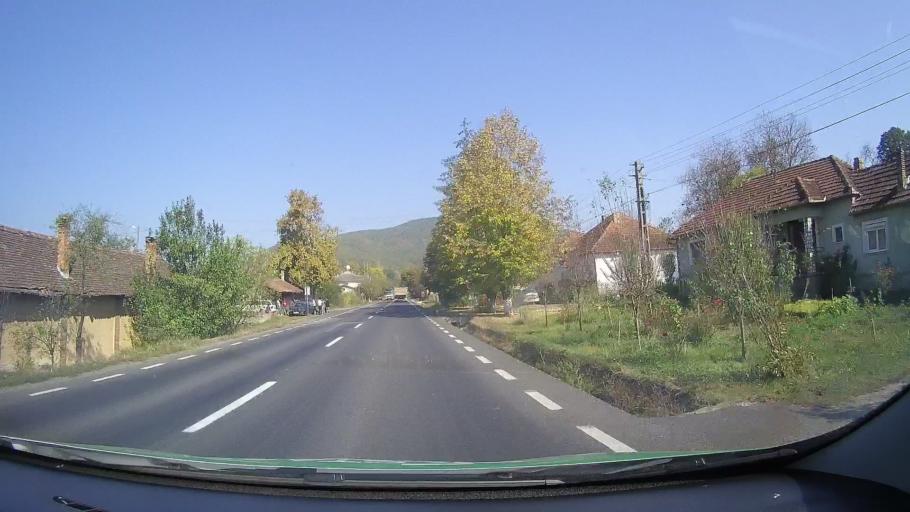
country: RO
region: Hunedoara
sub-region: Comuna Zam
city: Zam
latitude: 45.9990
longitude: 22.4400
